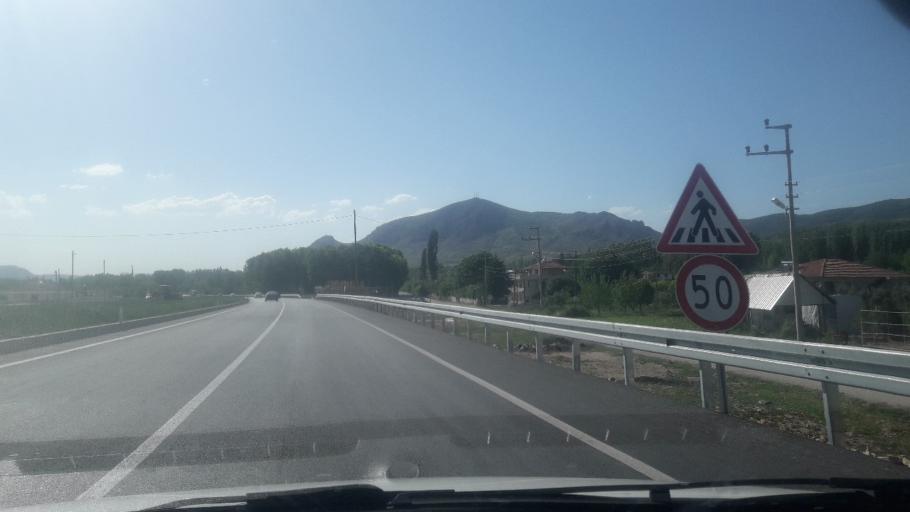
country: TR
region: Tokat
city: Dokmetepe
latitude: 40.3213
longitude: 36.2312
